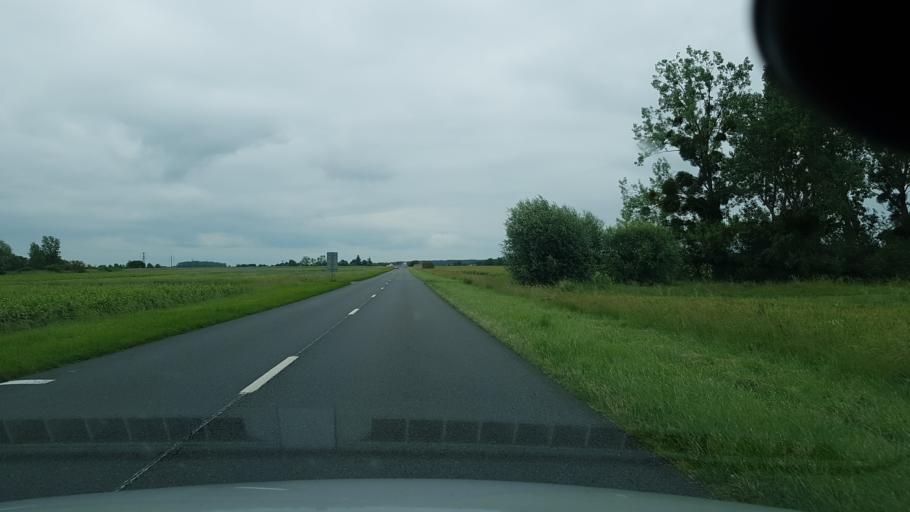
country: FR
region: Centre
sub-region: Departement du Loir-et-Cher
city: Chatillon-sur-Cher
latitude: 47.3173
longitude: 1.4989
